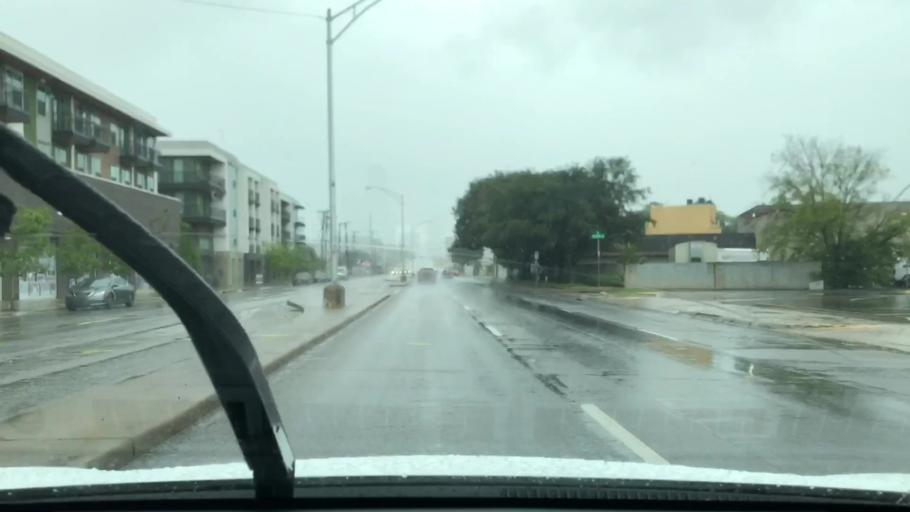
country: US
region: Texas
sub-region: Dallas County
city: Dallas
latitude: 32.7736
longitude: -96.8289
